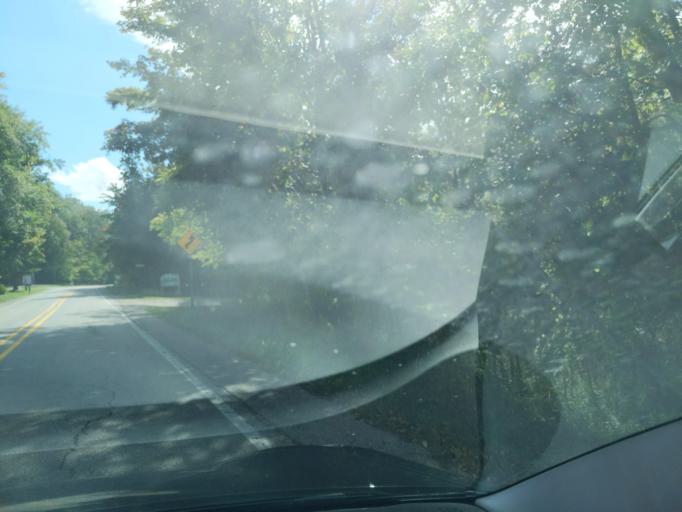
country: US
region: Michigan
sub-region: Antrim County
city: Bellaire
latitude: 45.0655
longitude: -85.3174
